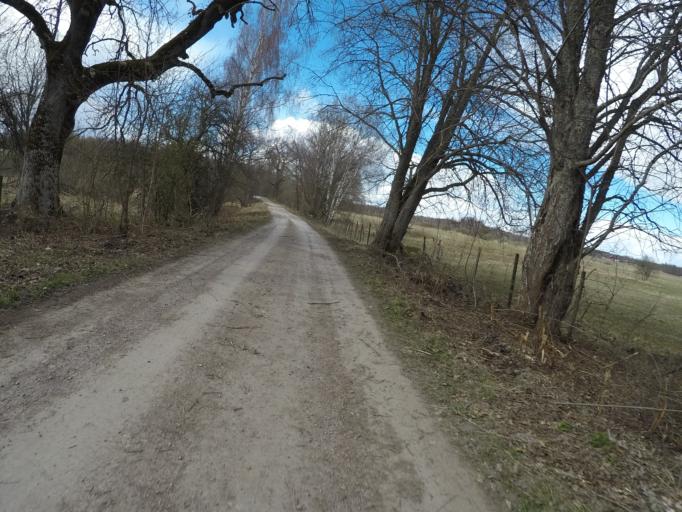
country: SE
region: Soedermanland
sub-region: Eskilstuna Kommun
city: Kvicksund
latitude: 59.4821
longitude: 16.2919
